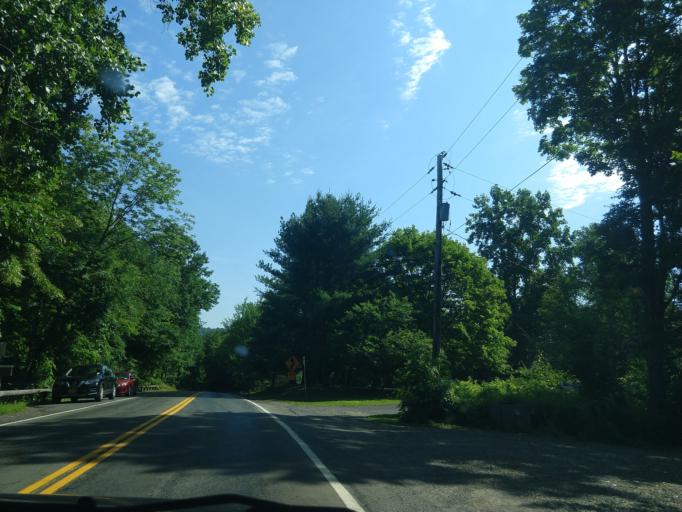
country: US
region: New York
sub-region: Tompkins County
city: East Ithaca
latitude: 42.4054
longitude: -76.4607
